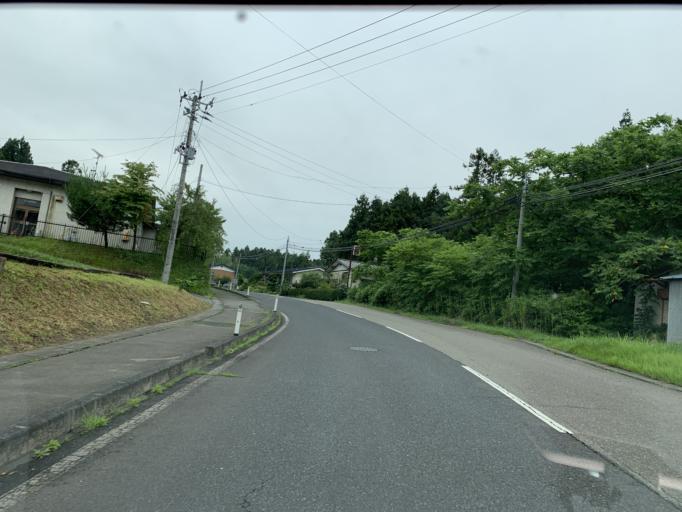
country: JP
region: Iwate
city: Ichinoseki
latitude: 38.8134
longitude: 141.1962
